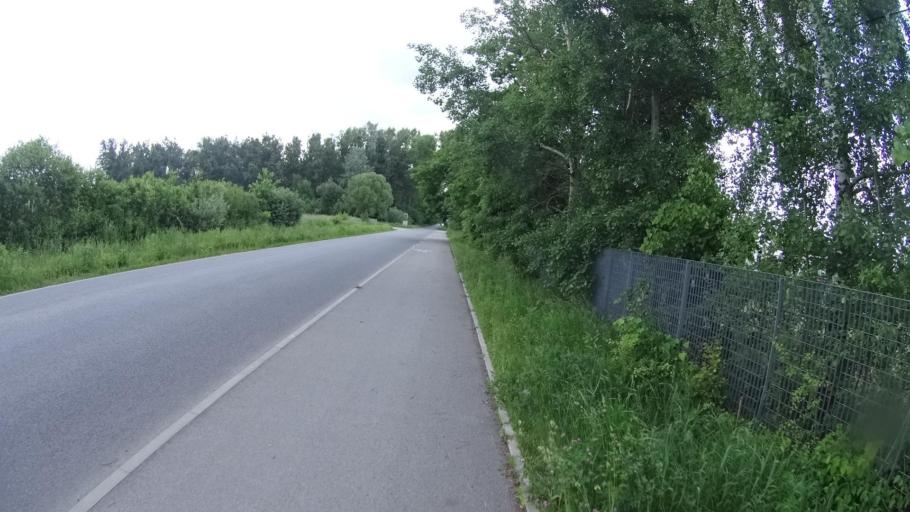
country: PL
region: Masovian Voivodeship
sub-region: Powiat pruszkowski
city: Nadarzyn
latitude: 52.0777
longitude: 20.8177
